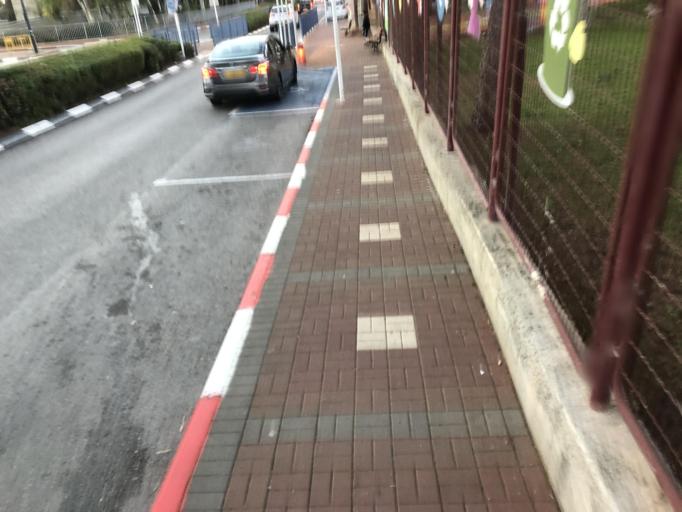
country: IL
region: Northern District
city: `Akko
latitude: 32.9368
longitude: 35.0912
